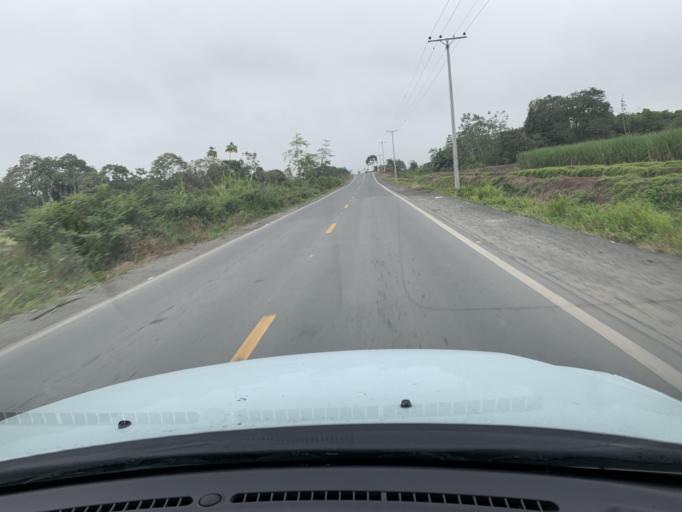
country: EC
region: Guayas
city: Coronel Marcelino Mariduena
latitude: -2.3334
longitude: -79.5279
